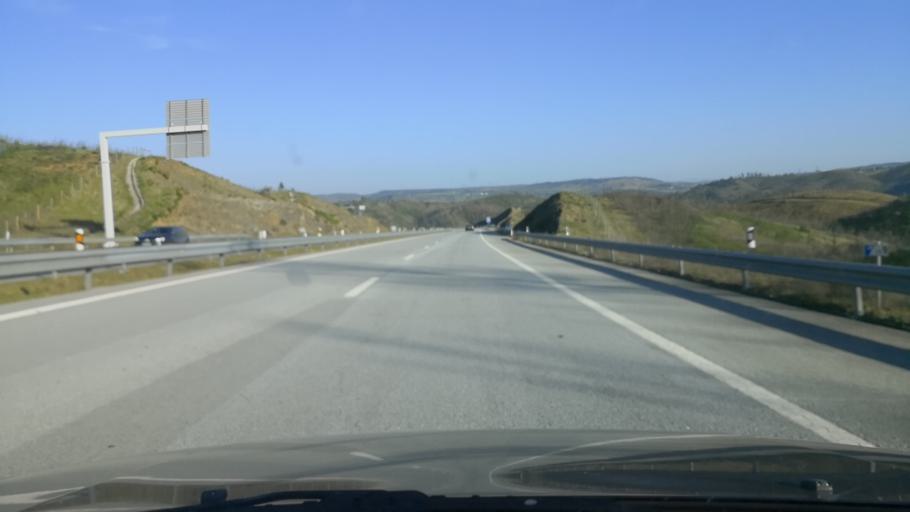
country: PT
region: Portalegre
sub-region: Gaviao
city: Gaviao
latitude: 39.5504
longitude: -7.8361
